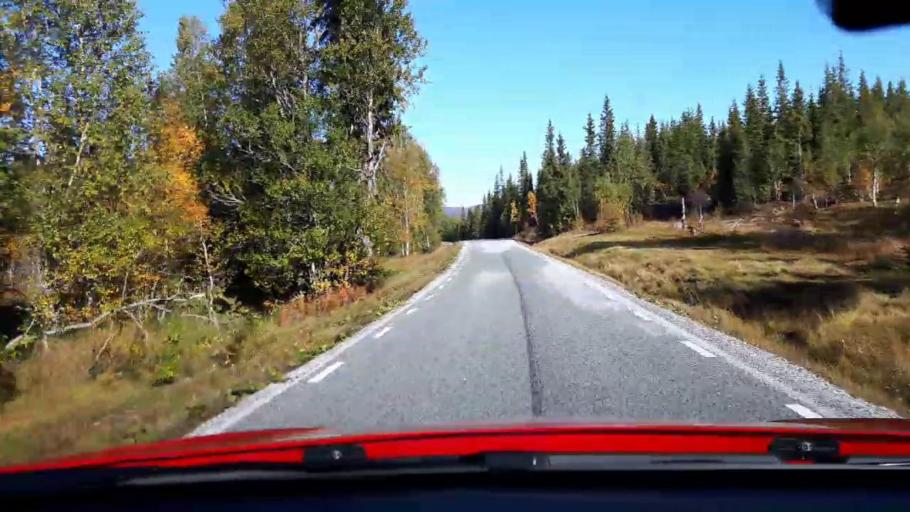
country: NO
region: Nord-Trondelag
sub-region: Lierne
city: Sandvika
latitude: 64.6200
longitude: 13.6973
